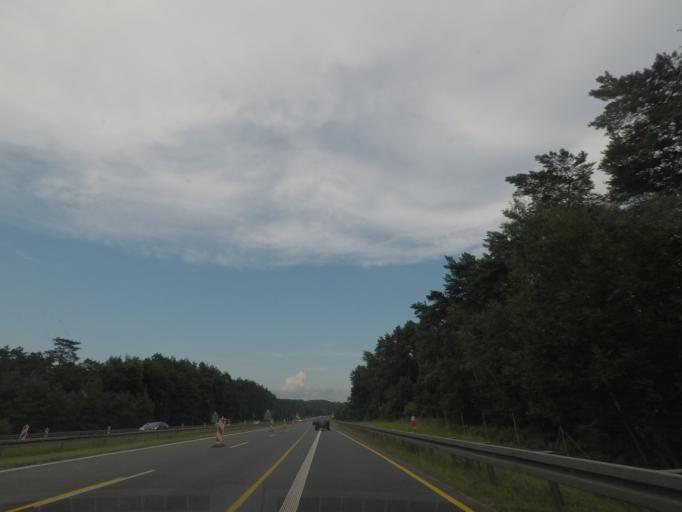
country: PL
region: Lesser Poland Voivodeship
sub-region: Powiat krakowski
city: Sanka
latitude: 50.0939
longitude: 19.6513
